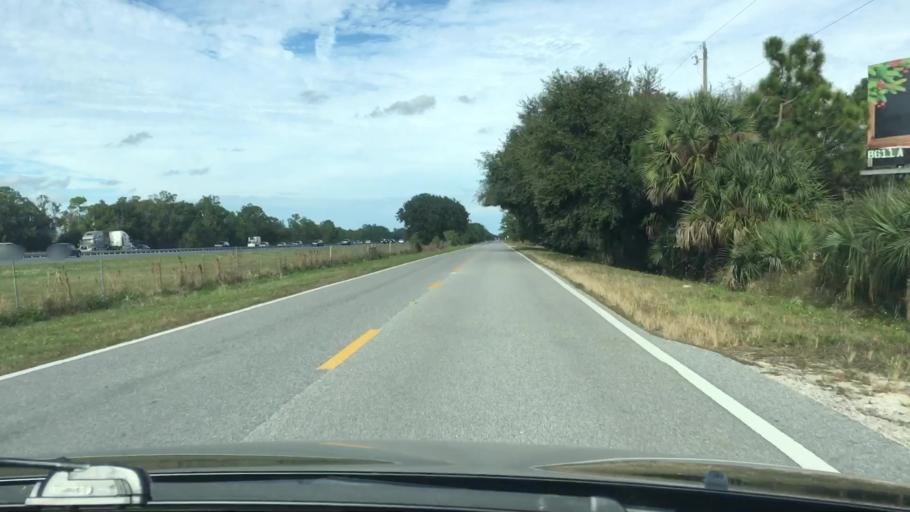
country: US
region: Florida
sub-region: Volusia County
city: Ormond-by-the-Sea
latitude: 29.3058
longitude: -81.1312
